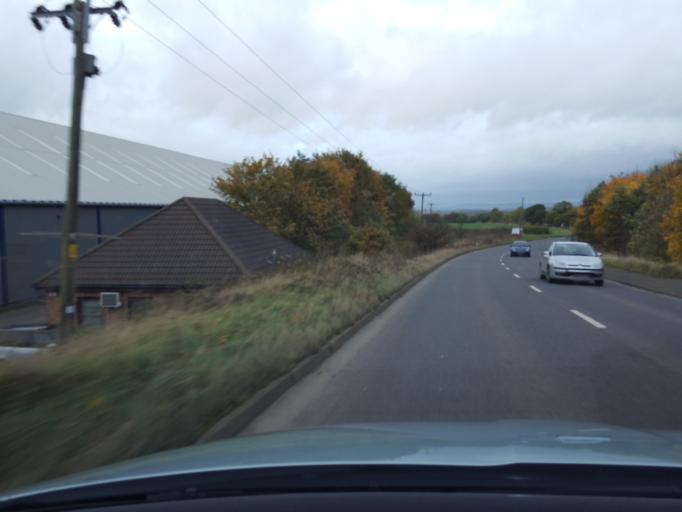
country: GB
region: Scotland
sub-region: Edinburgh
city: Newbridge
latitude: 55.9146
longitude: -3.4082
